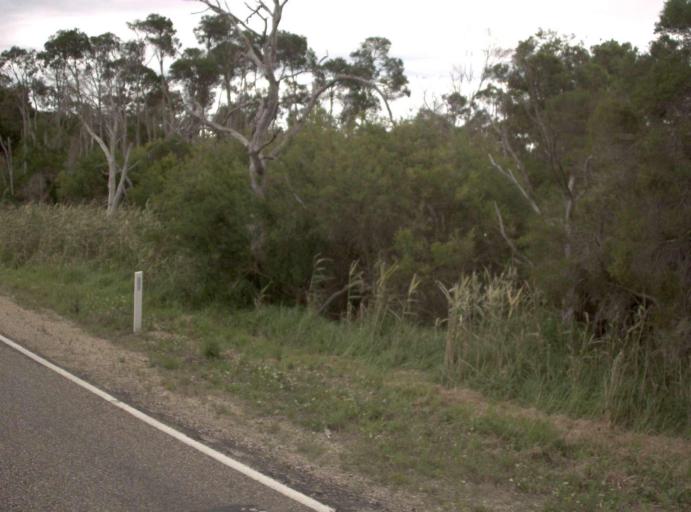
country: AU
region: Victoria
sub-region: Wellington
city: Sale
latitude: -38.0140
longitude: 147.1886
